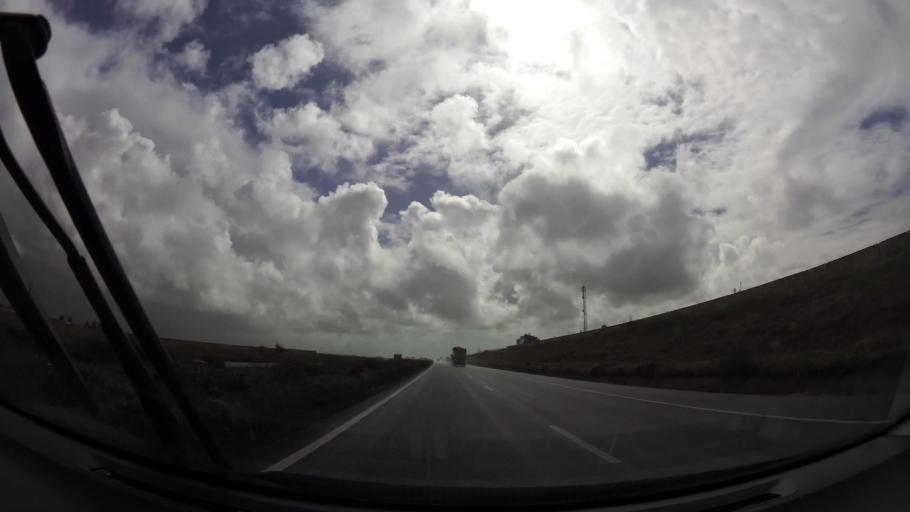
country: MA
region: Grand Casablanca
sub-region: Nouaceur
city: Dar Bouazza
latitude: 33.3834
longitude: -7.8920
